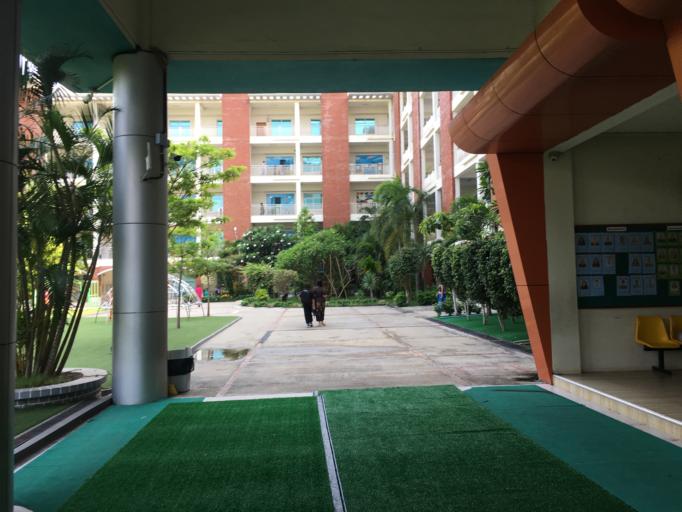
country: MM
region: Mandalay
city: Mandalay
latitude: 21.9689
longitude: 96.1293
